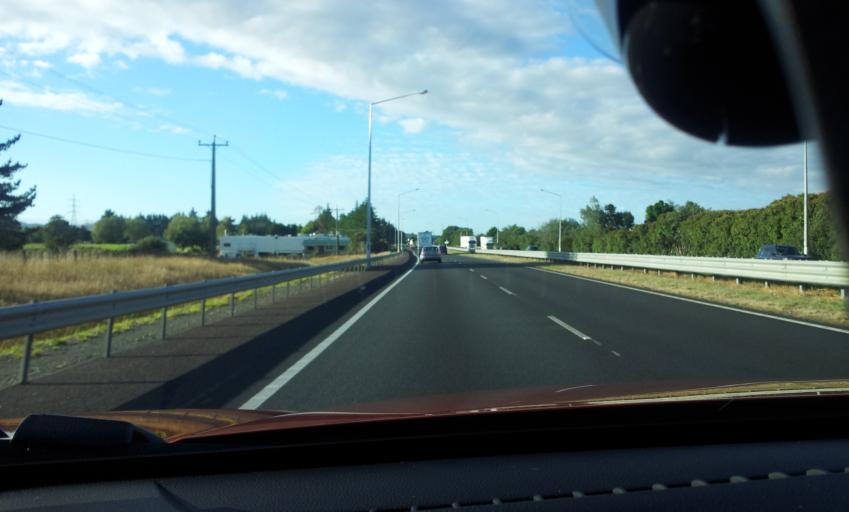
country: NZ
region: Auckland
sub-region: Auckland
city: Papakura
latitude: -37.1117
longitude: 174.9474
